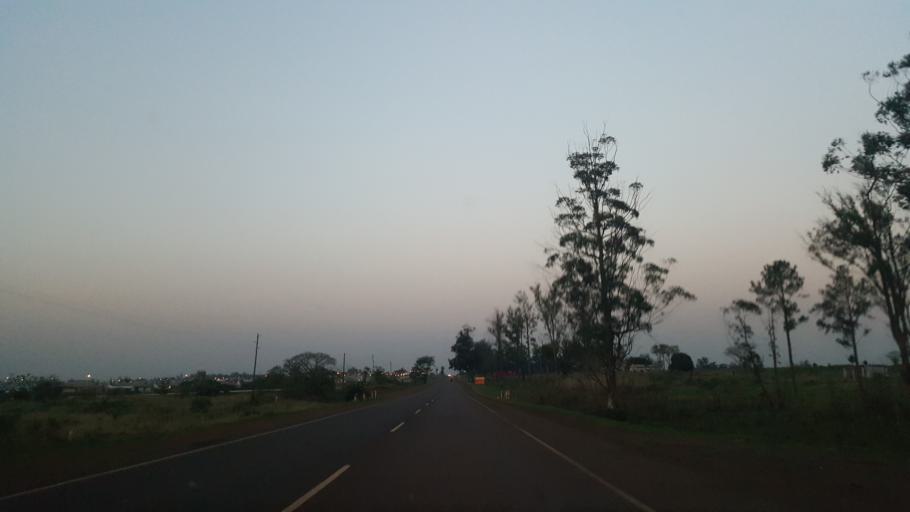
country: AR
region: Misiones
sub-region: Departamento de Capital
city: Posadas
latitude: -27.4173
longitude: -55.9882
